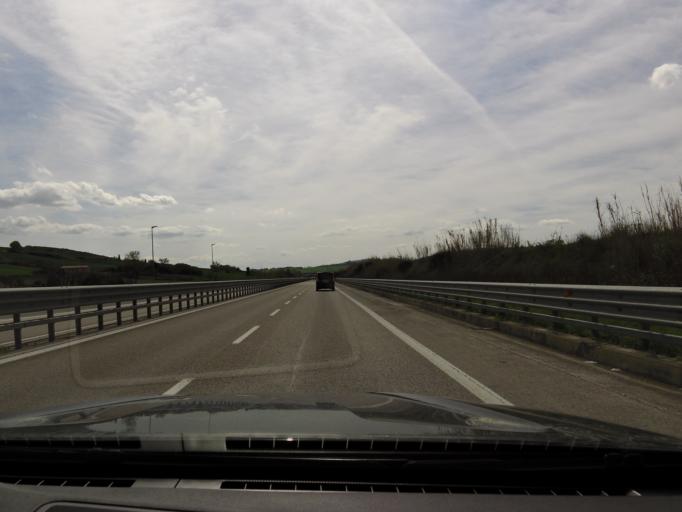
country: IT
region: The Marches
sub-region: Provincia di Ancona
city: San Biagio
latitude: 43.5514
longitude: 13.5170
